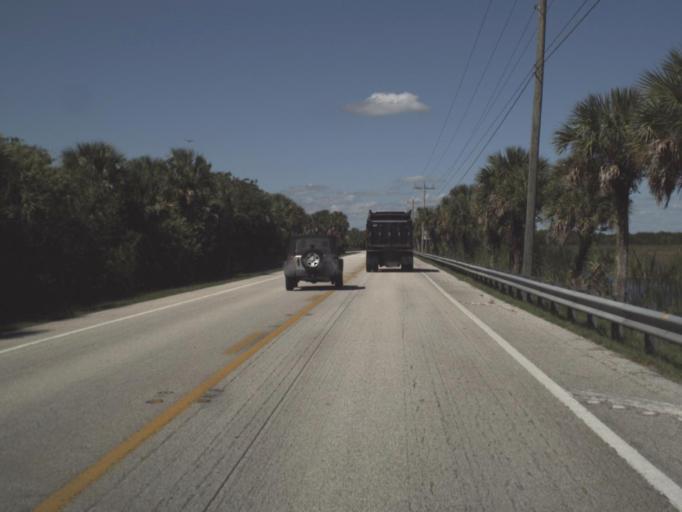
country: US
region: Florida
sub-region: Collier County
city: Marco
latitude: 25.9323
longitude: -81.4444
